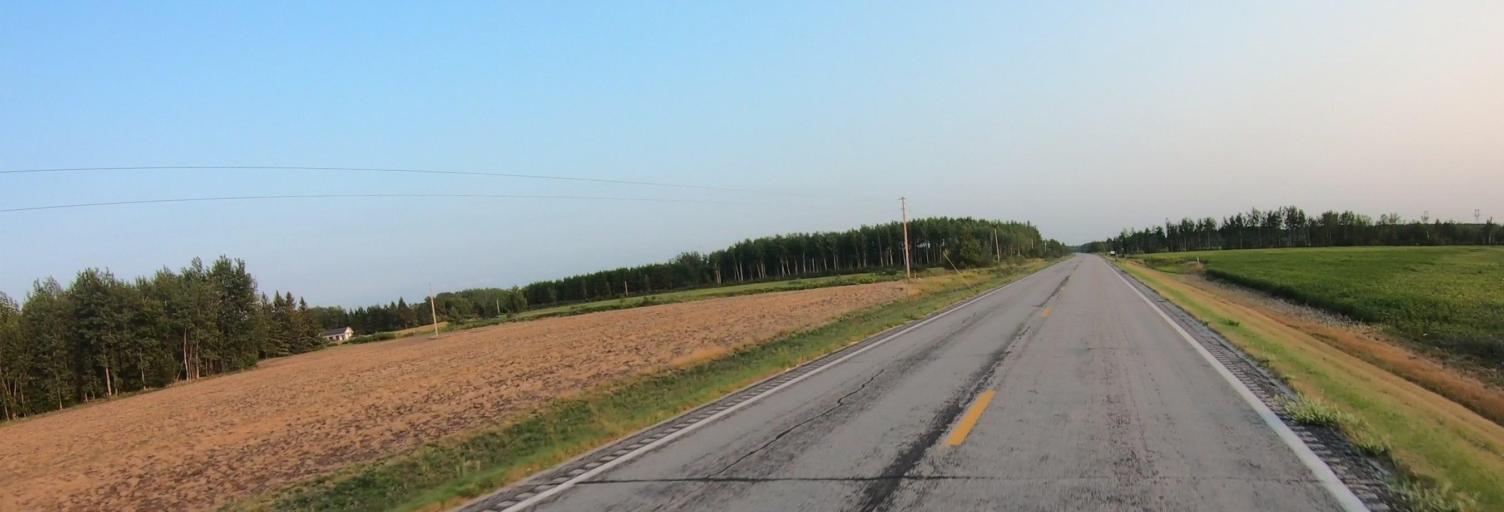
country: US
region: Minnesota
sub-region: Roseau County
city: Warroad
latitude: 48.7668
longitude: -95.3309
